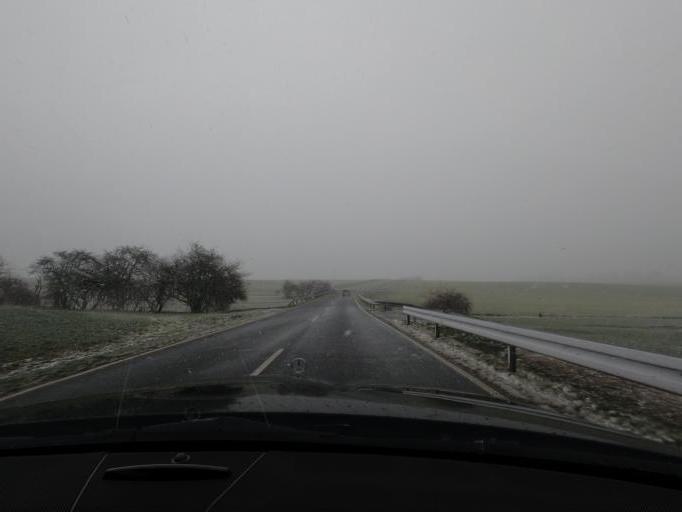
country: DE
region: Thuringia
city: Kullstedt
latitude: 51.2856
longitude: 10.2908
